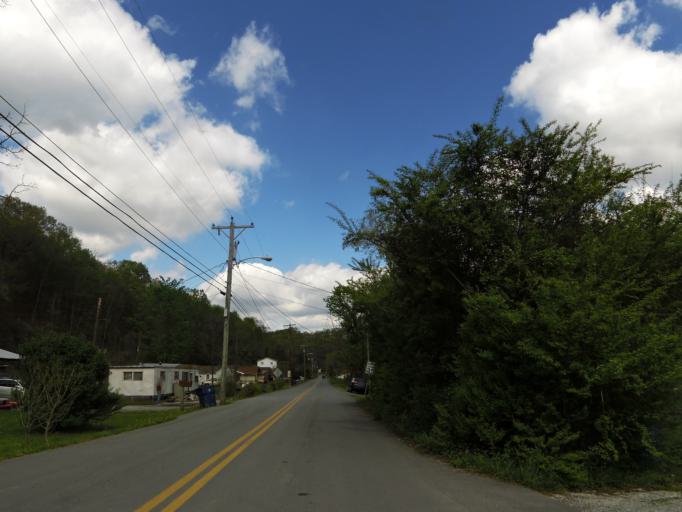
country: US
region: Kentucky
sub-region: Bell County
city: Middlesboro
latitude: 36.6153
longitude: -83.7649
